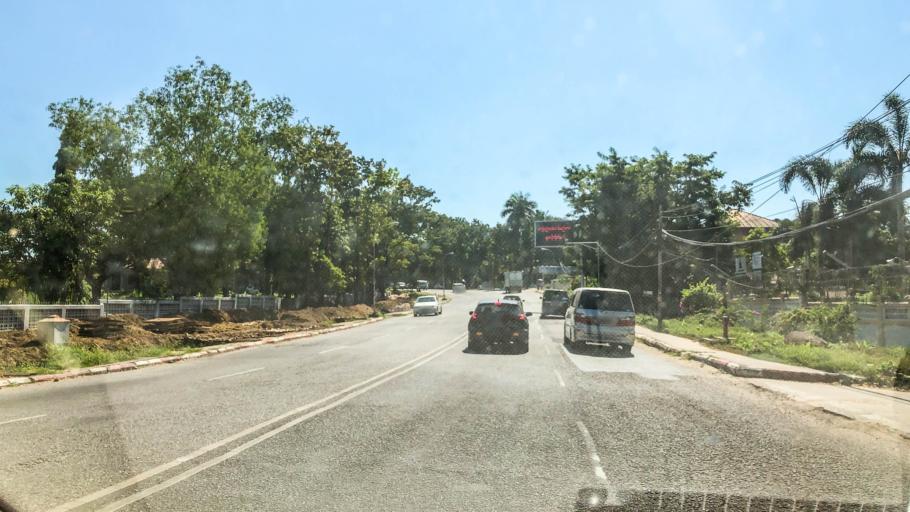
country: MM
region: Yangon
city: Yangon
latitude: 16.8920
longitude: 96.1317
